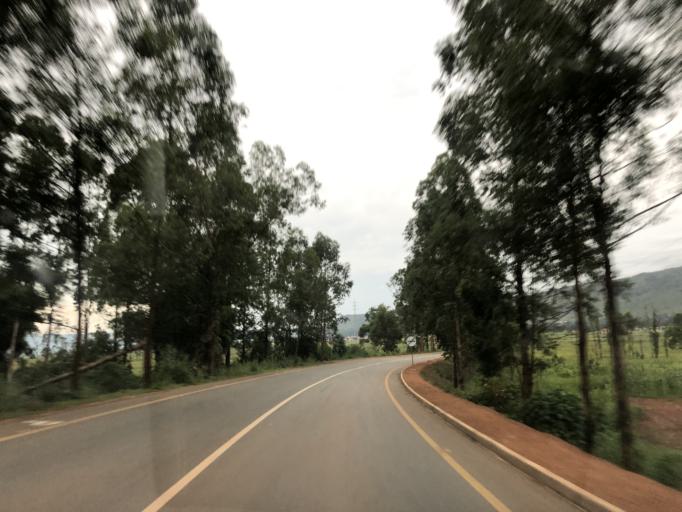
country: AO
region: Cuanza Sul
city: Uacu Cungo
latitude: -11.3350
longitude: 15.1025
